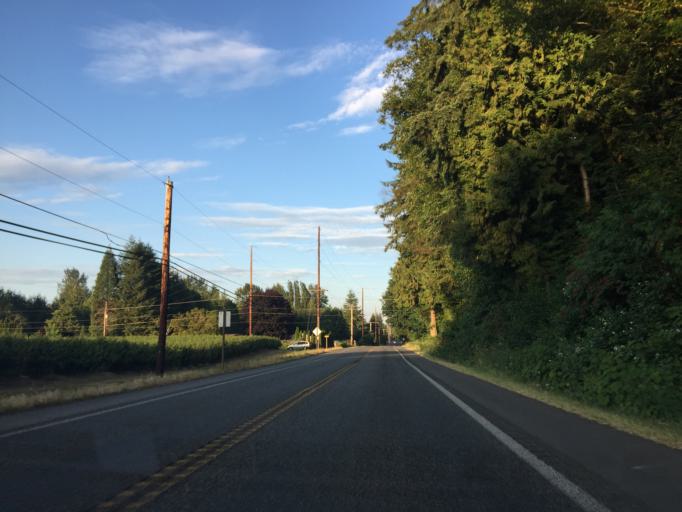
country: US
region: Washington
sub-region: Whatcom County
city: Ferndale
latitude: 48.9353
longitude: -122.6291
